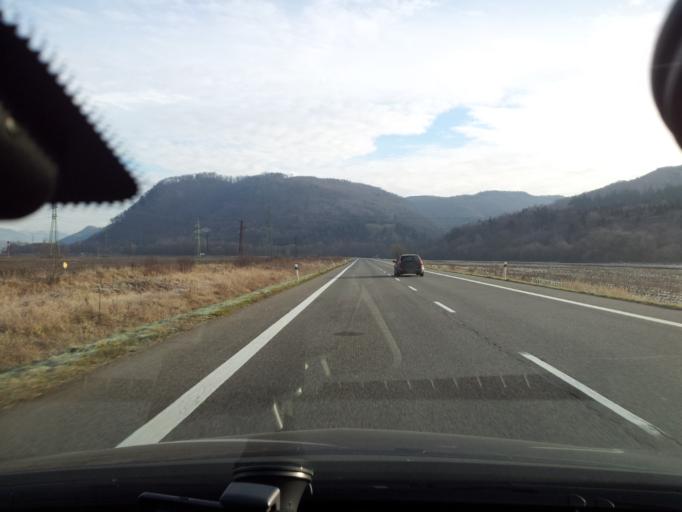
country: SK
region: Banskobystricky
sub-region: Okres Banska Bystrica
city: Banska Bystrica
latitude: 48.7462
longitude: 19.2423
